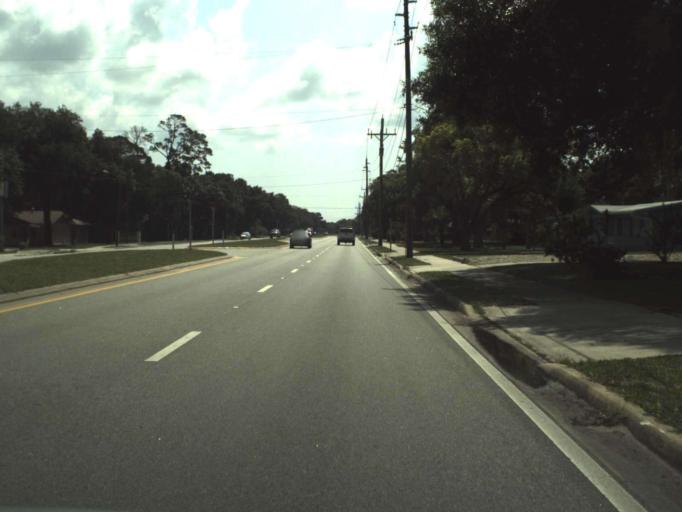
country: US
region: Florida
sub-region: Volusia County
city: Glencoe
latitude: 29.0133
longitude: -80.9555
